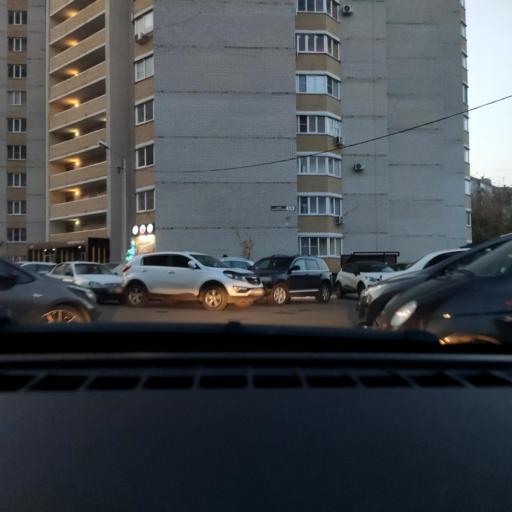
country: RU
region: Voronezj
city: Voronezh
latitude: 51.6824
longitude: 39.2518
